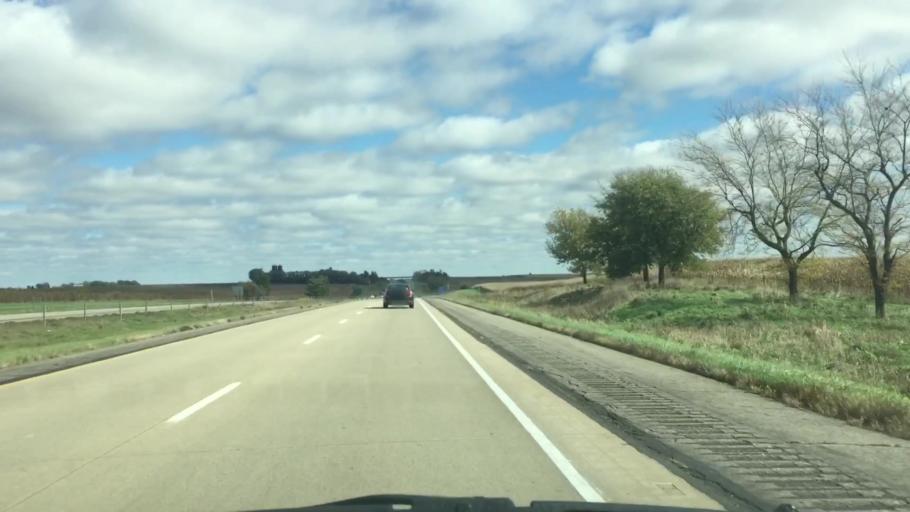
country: US
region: Iowa
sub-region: Poweshiek County
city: Brooklyn
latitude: 41.6962
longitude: -92.2588
